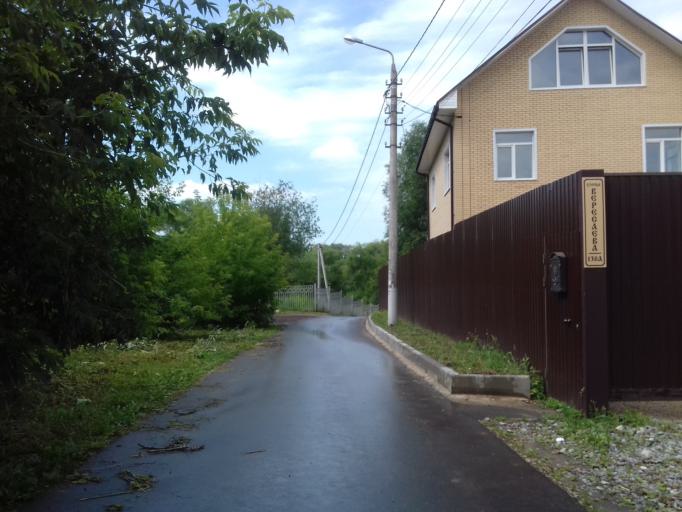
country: RU
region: Tula
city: Tula
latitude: 54.1857
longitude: 37.5814
